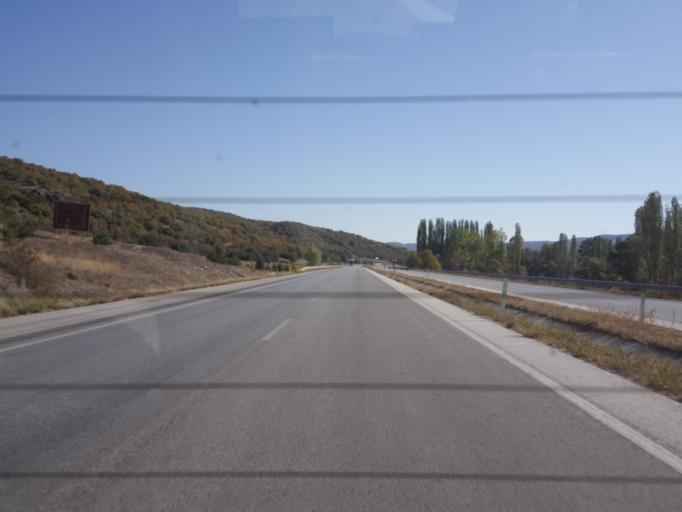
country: TR
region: Corum
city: Alaca
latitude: 40.3153
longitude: 34.6700
